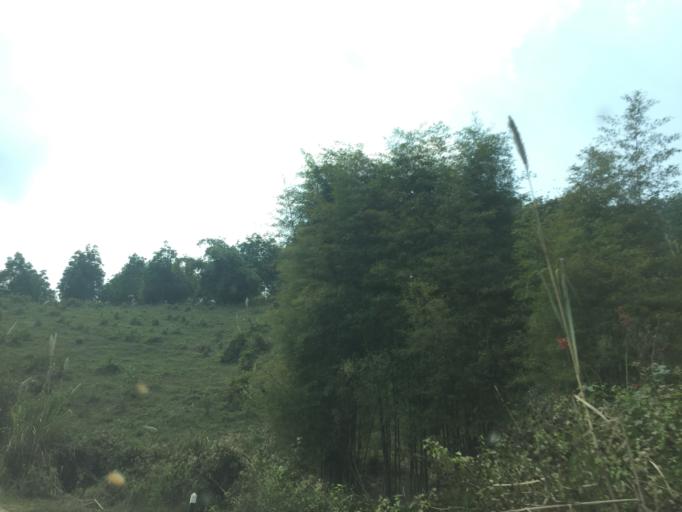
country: TH
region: Nan
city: Song Khwae
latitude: 19.7437
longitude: 100.7072
